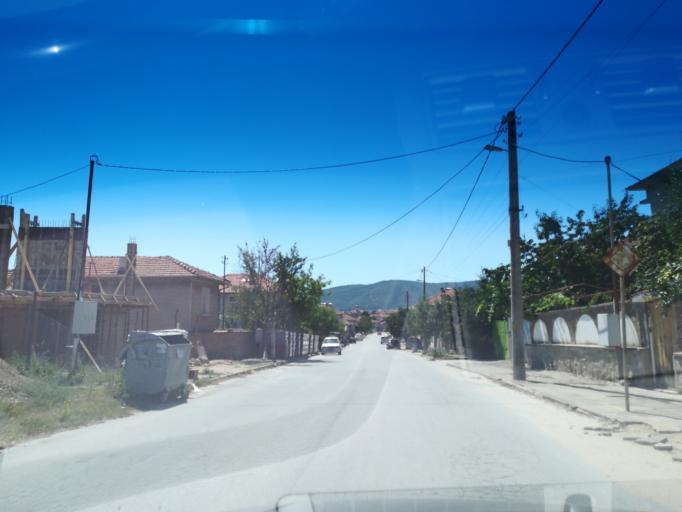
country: BG
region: Pazardzhik
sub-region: Obshtina Strelcha
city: Strelcha
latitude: 42.5147
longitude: 24.3216
